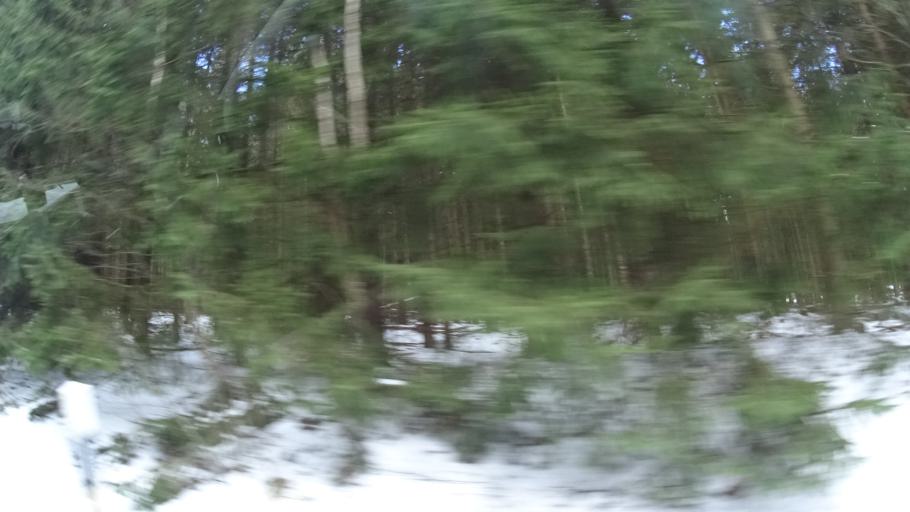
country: DE
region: Thuringia
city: Benshausen
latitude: 50.6218
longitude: 10.6292
